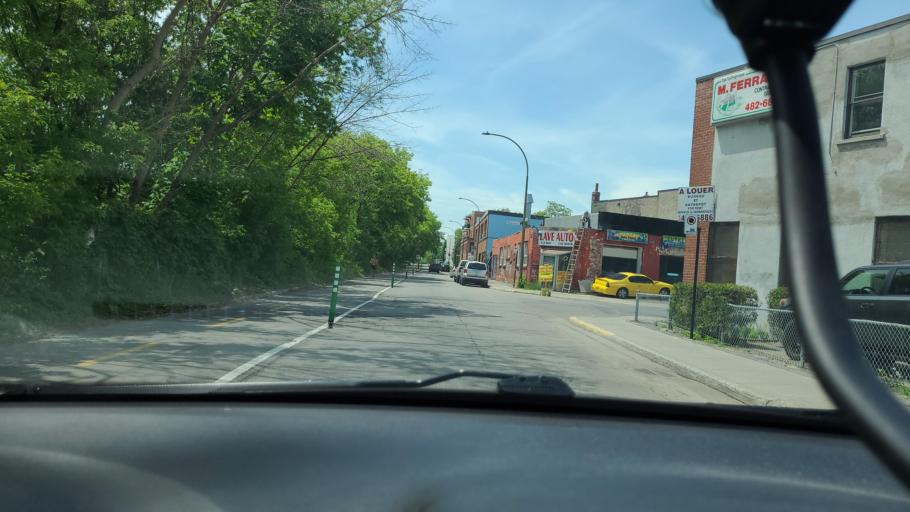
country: CA
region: Quebec
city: Saint-Raymond
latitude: 45.4664
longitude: -73.6178
